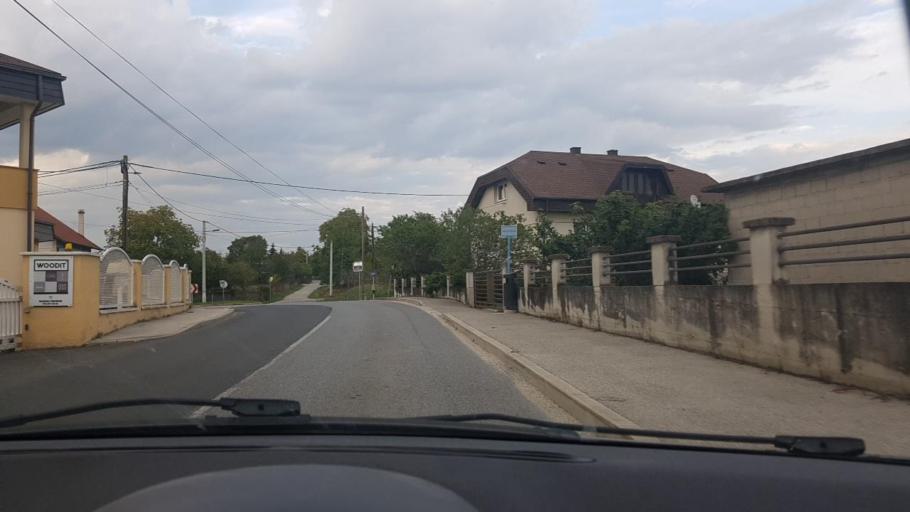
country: HR
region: Grad Zagreb
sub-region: Sesvete
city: Sesvete
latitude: 45.8862
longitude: 16.1747
